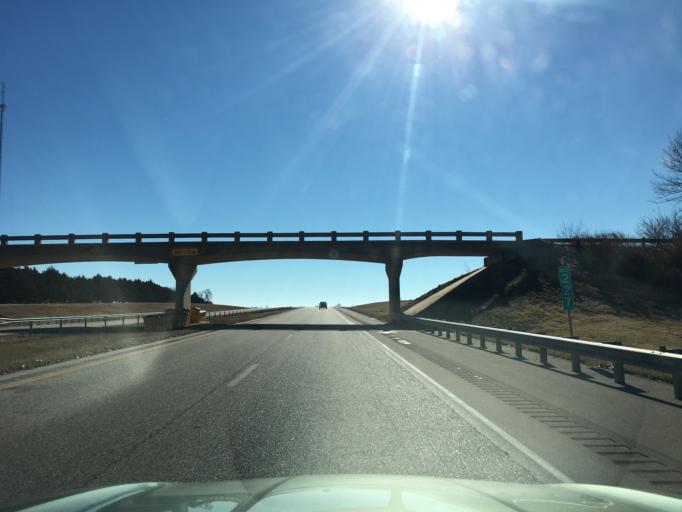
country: US
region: Oklahoma
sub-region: Kay County
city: Blackwell
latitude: 36.8701
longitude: -97.3490
